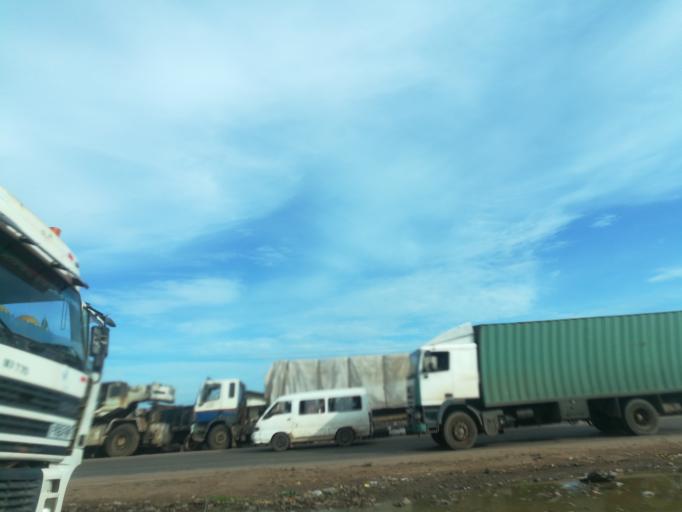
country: NG
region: Oyo
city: Ibadan
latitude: 7.3687
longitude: 3.9281
